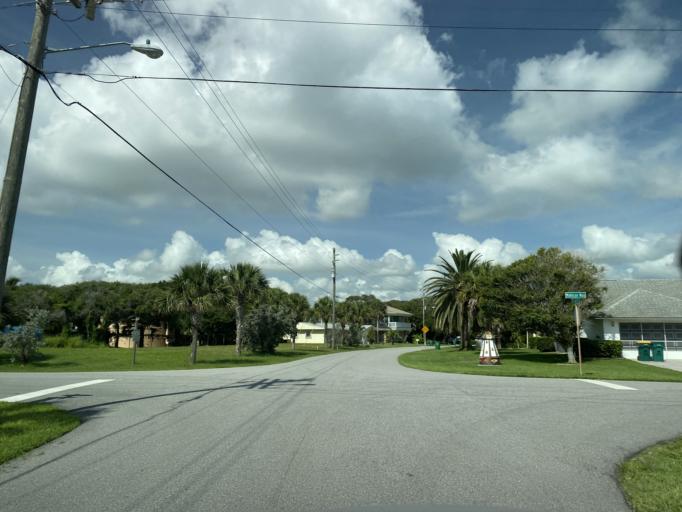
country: US
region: Florida
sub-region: Brevard County
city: Micco
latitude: 27.9284
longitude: -80.4881
